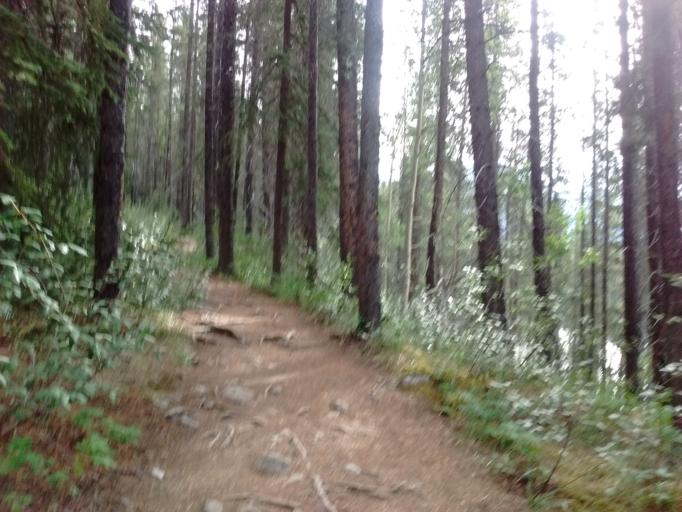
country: CA
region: Alberta
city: Jasper Park Lodge
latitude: 52.5278
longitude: -117.6536
